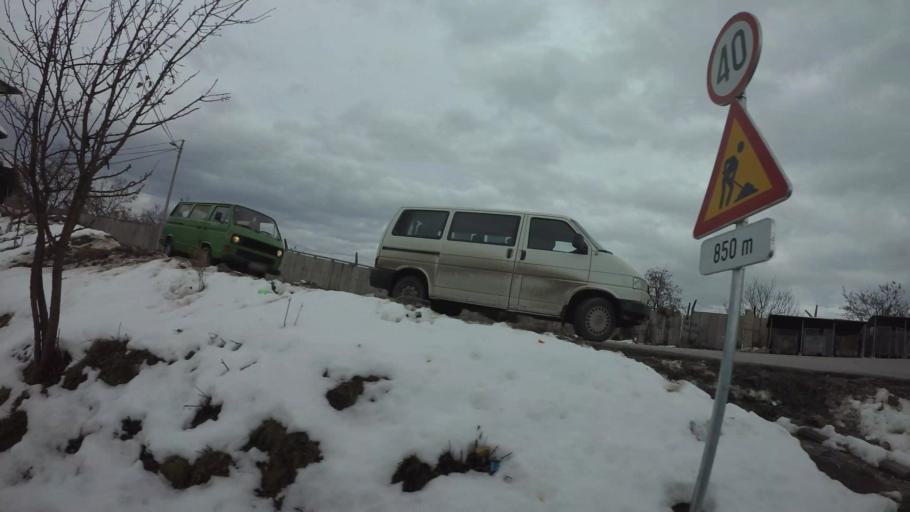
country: BA
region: Federation of Bosnia and Herzegovina
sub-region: Kanton Sarajevo
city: Sarajevo
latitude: 43.8615
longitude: 18.3381
